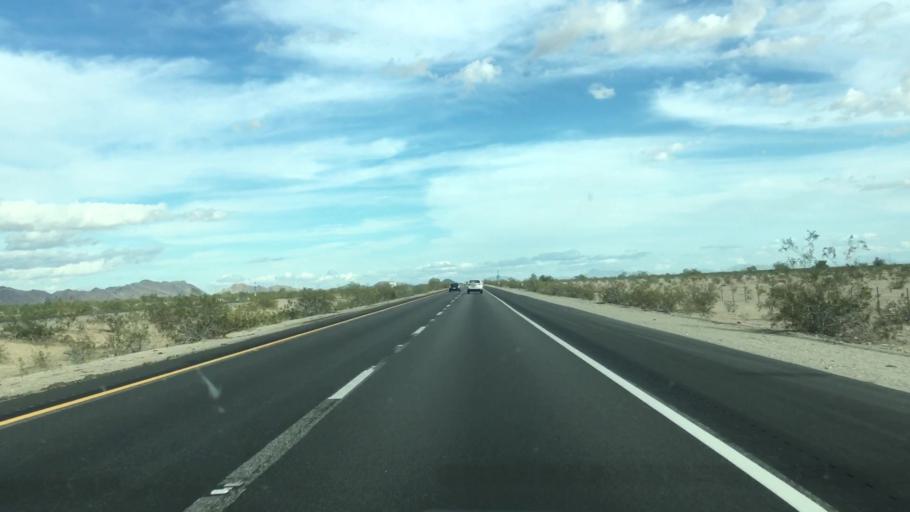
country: US
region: California
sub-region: Riverside County
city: Mesa Verde
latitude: 33.6092
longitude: -114.8526
